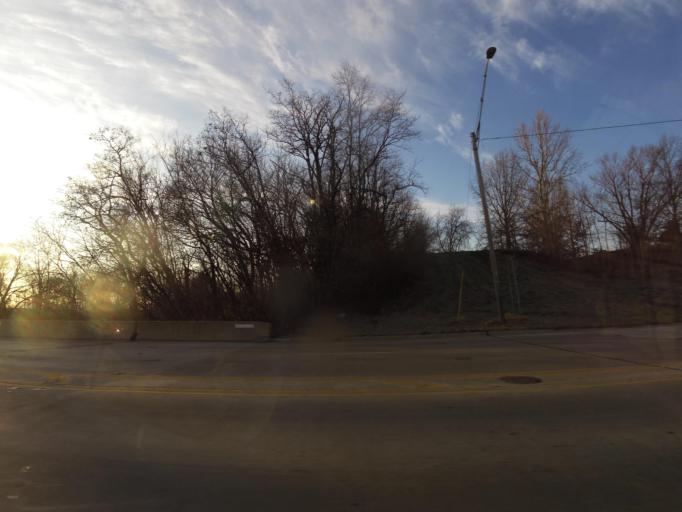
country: US
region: Illinois
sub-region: Fayette County
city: Vandalia
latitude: 38.9606
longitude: -89.0887
